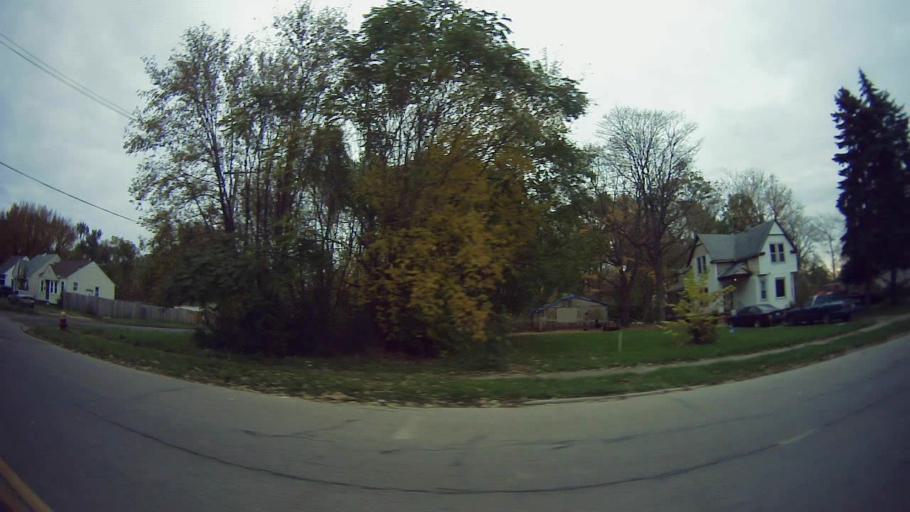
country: US
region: Michigan
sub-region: Wayne County
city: Dearborn
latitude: 42.3556
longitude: -83.1872
